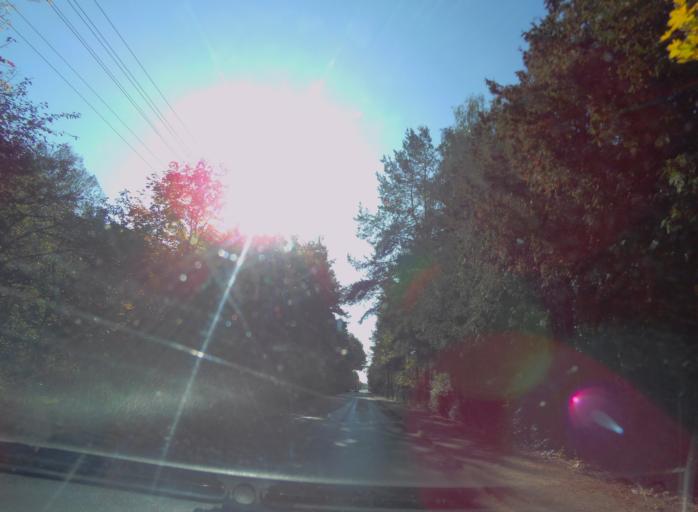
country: PL
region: Masovian Voivodeship
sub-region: Powiat otwocki
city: Jozefow
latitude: 52.1706
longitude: 21.3015
